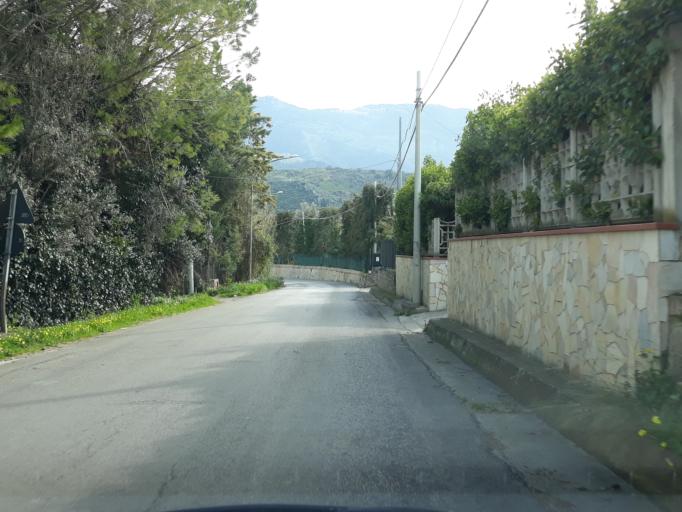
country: IT
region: Sicily
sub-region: Palermo
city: Monreale
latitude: 38.0714
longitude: 13.3041
